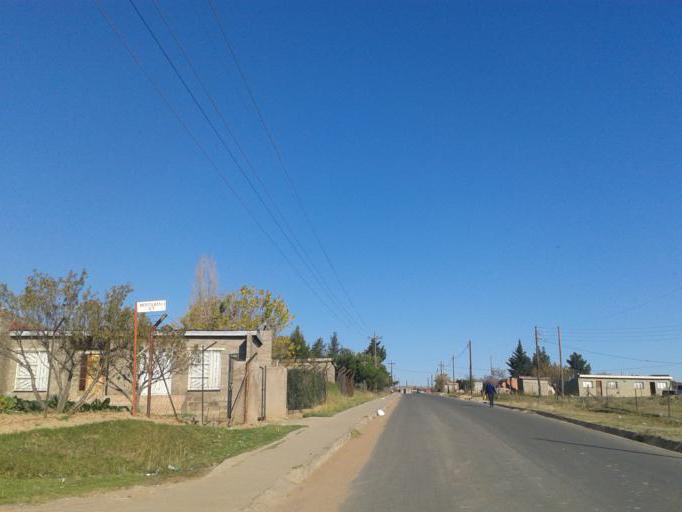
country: LS
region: Maseru
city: Maseru
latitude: -29.2810
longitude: 27.5353
